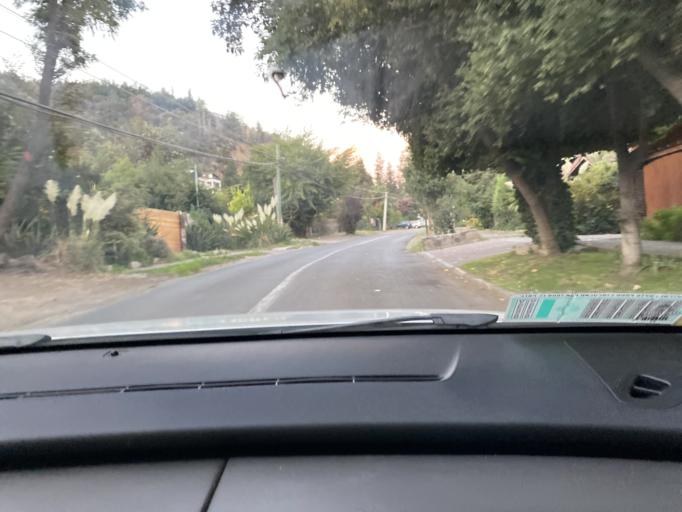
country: CL
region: Santiago Metropolitan
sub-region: Provincia de Santiago
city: Villa Presidente Frei, Nunoa, Santiago, Chile
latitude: -33.3576
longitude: -70.4835
